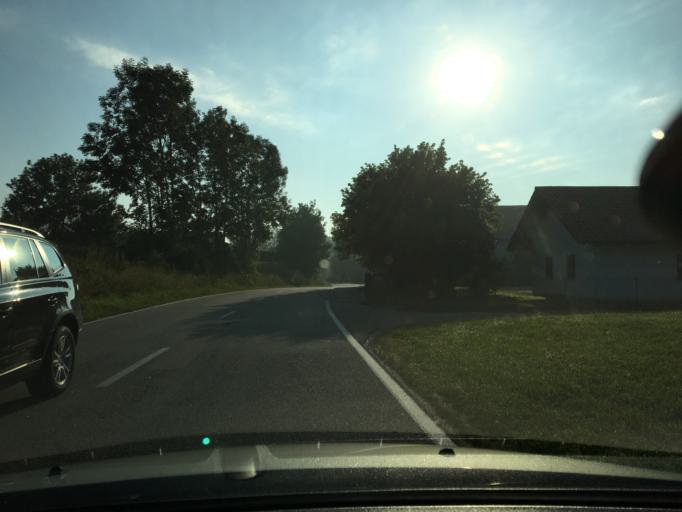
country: DE
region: Bavaria
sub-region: Lower Bavaria
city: Geisenhausen
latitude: 48.4798
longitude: 12.2832
